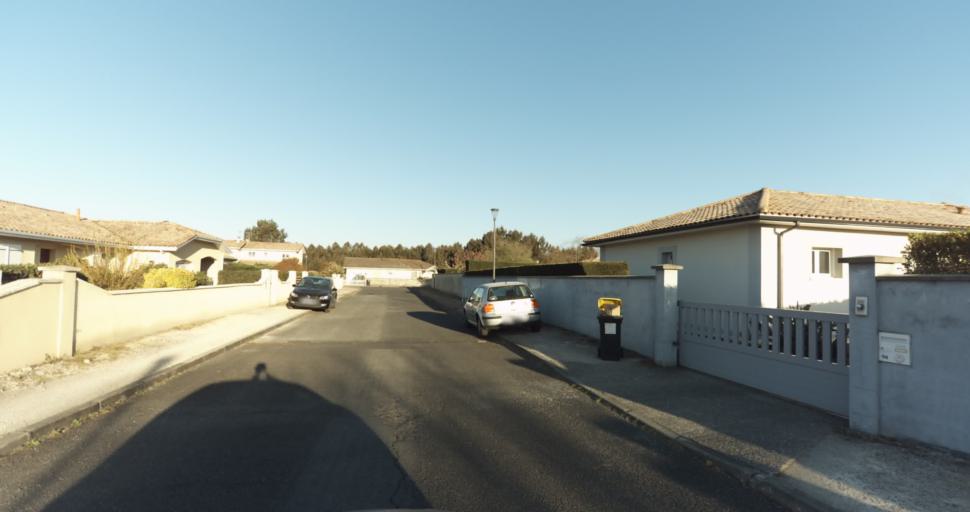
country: FR
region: Aquitaine
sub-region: Departement de la Gironde
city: Martignas-sur-Jalle
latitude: 44.8198
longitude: -0.7806
